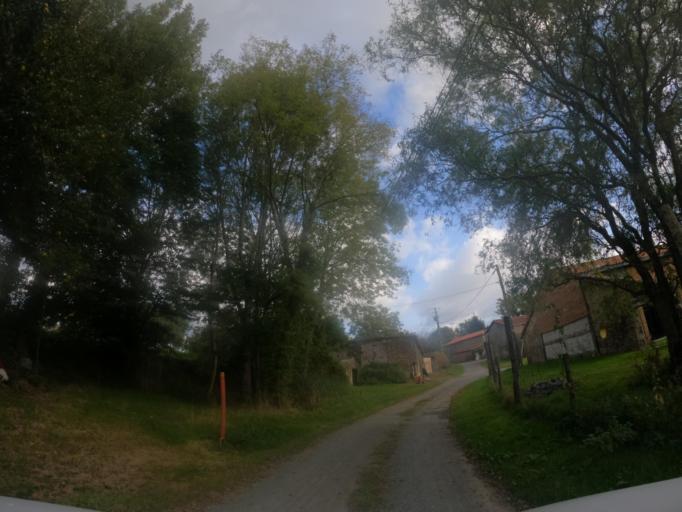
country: FR
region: Poitou-Charentes
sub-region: Departement des Deux-Sevres
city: La Foret-sur-Sevre
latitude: 46.7940
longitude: -0.6116
